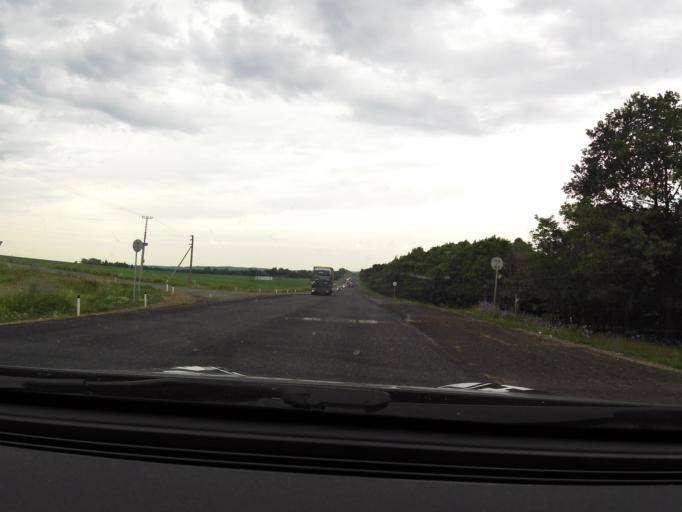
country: RU
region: Bashkortostan
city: Kudeyevskiy
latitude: 54.8034
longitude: 56.6173
